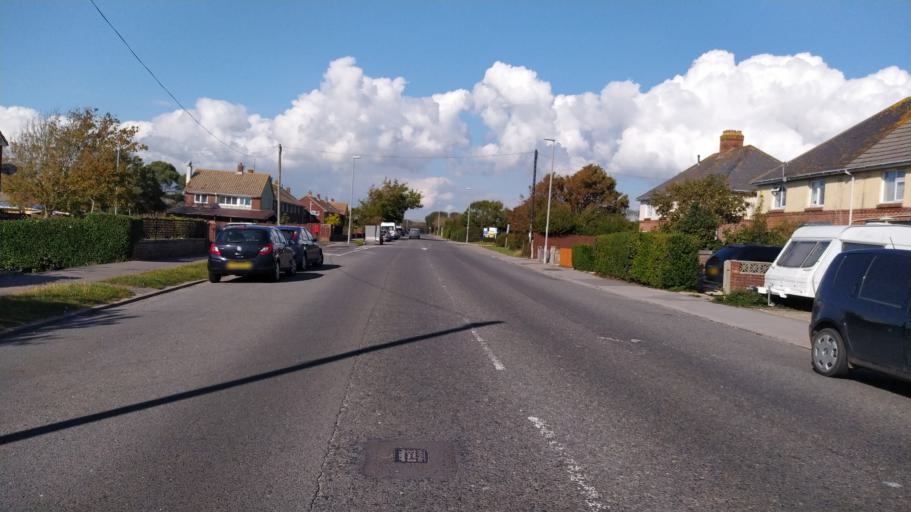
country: GB
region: England
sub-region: Dorset
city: Weymouth
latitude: 50.6136
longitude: -2.4817
